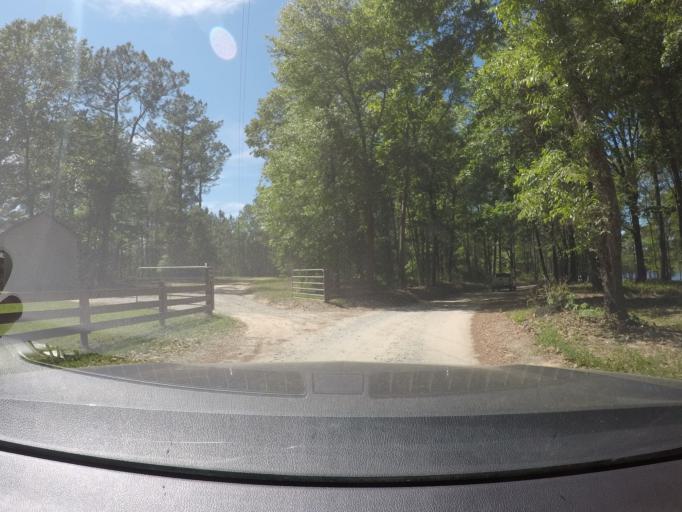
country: US
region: Georgia
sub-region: Evans County
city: Claxton
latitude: 32.1269
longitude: -81.7921
